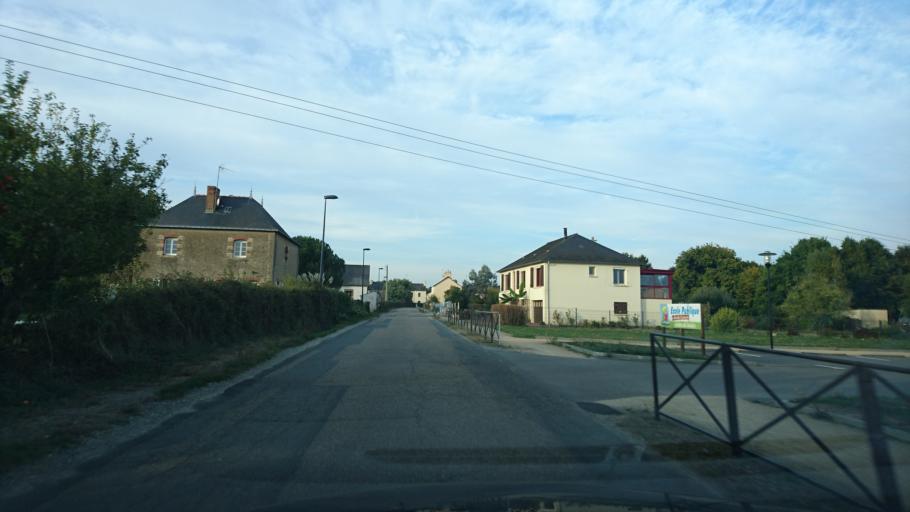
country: FR
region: Brittany
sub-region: Departement d'Ille-et-Vilaine
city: Sainte-Marie
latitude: 47.6906
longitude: -2.0034
